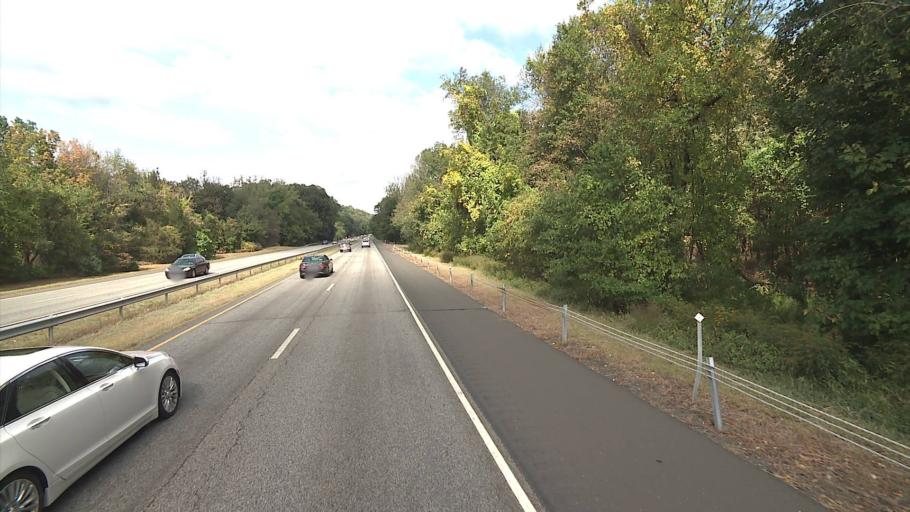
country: US
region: Connecticut
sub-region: New Haven County
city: Wallingford
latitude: 41.4485
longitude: -72.8421
